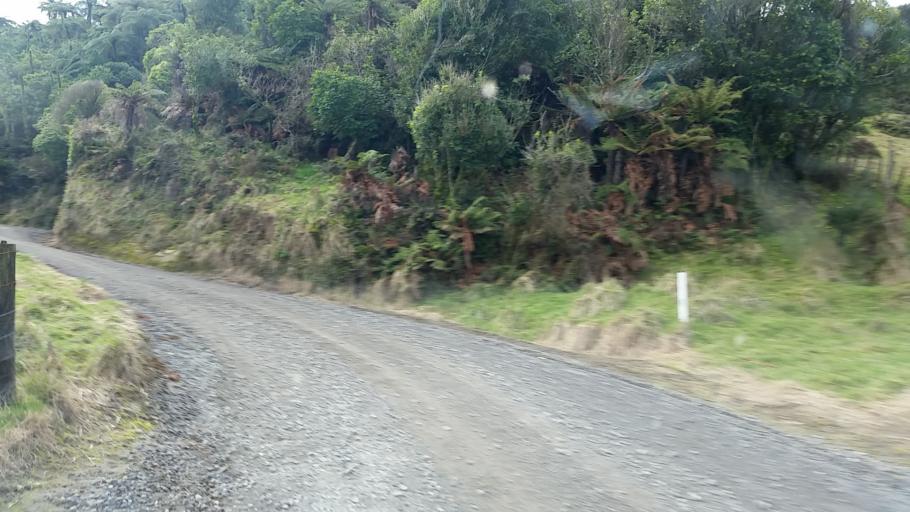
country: NZ
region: Taranaki
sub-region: South Taranaki District
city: Eltham
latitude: -39.1731
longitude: 174.6191
